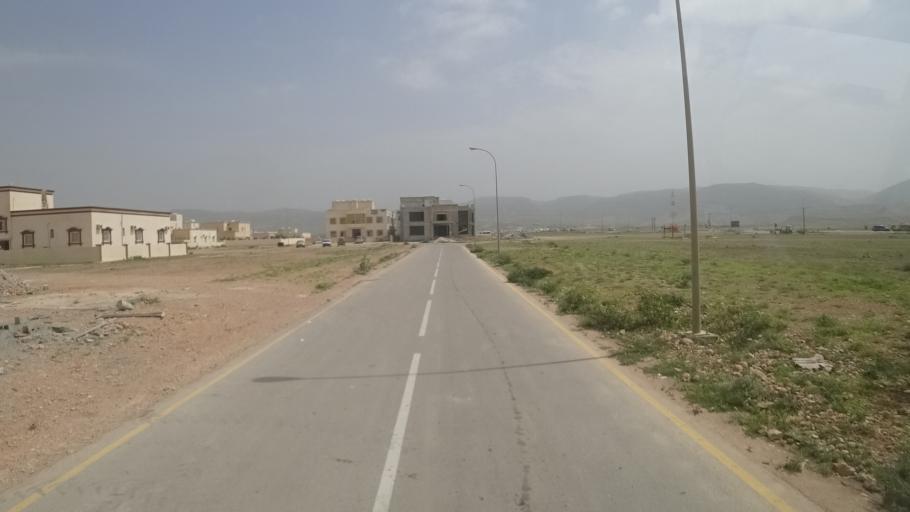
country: OM
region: Zufar
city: Salalah
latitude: 17.0988
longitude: 54.2157
